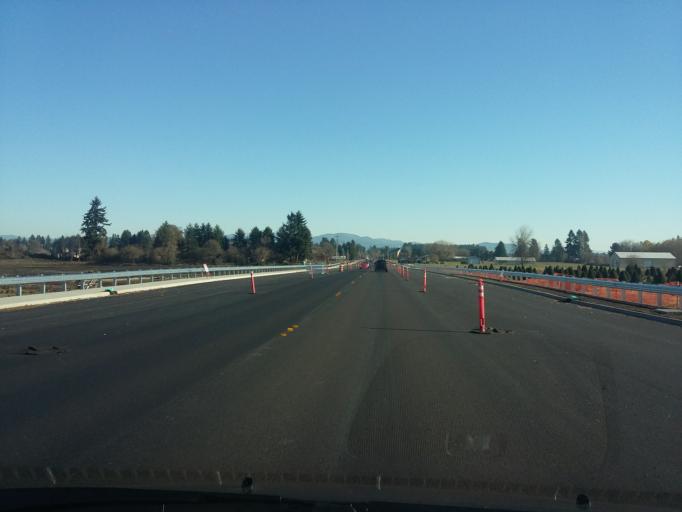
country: US
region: Washington
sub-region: Clark County
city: Barberton
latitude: 45.7078
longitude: -122.5929
